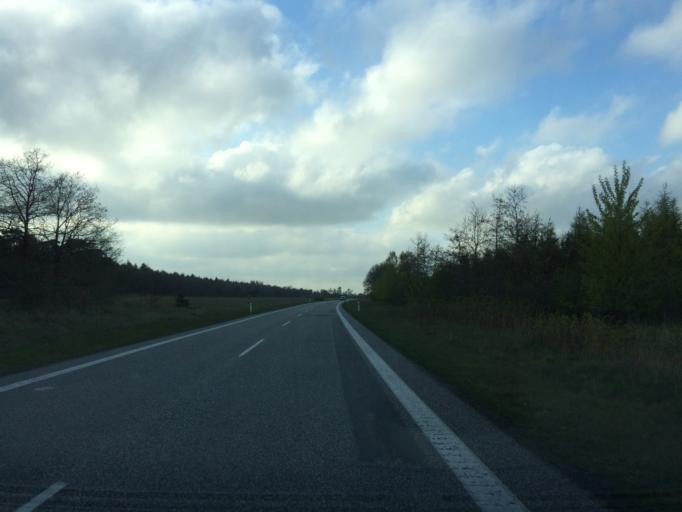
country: DK
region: Central Jutland
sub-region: Viborg Kommune
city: Karup
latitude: 56.3160
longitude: 9.1202
